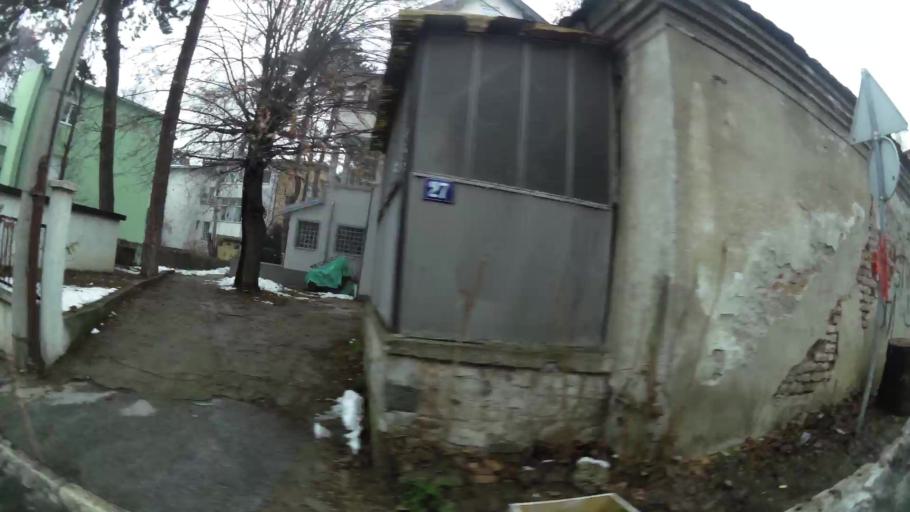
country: RS
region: Central Serbia
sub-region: Belgrade
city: Savski Venac
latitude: 44.7928
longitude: 20.4457
